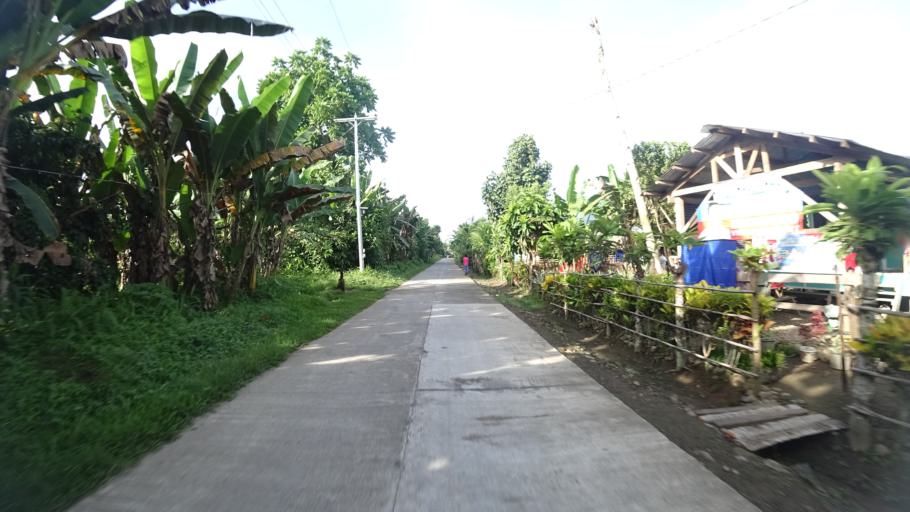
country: PH
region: Eastern Visayas
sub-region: Province of Leyte
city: Pastrana
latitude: 11.1723
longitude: 124.8717
